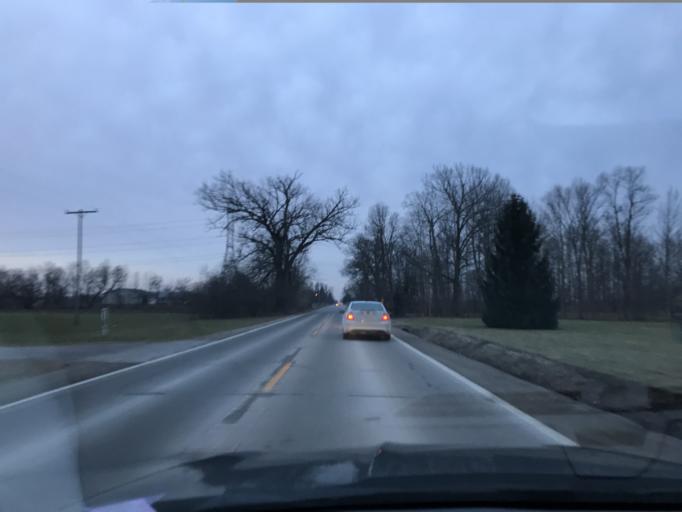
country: US
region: Michigan
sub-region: Macomb County
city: Romeo
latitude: 42.8291
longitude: -82.9635
